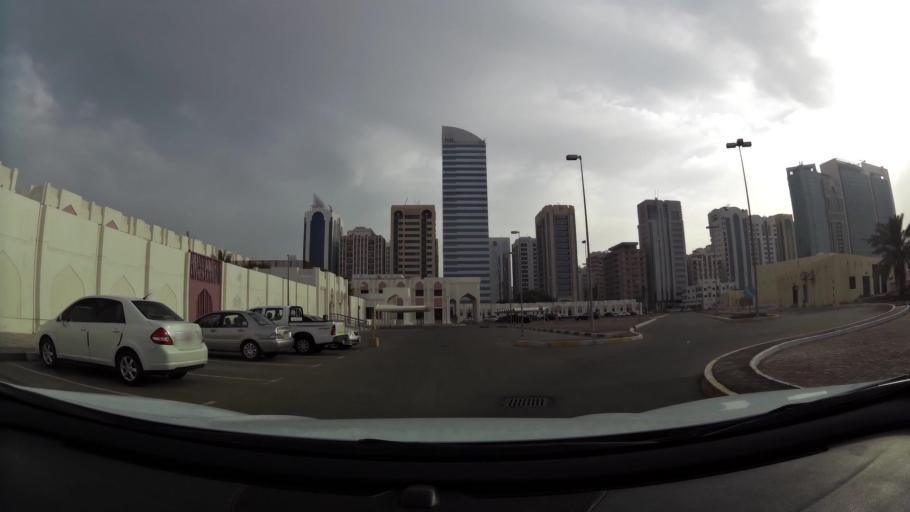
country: AE
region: Abu Dhabi
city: Abu Dhabi
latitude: 24.4718
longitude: 54.3653
